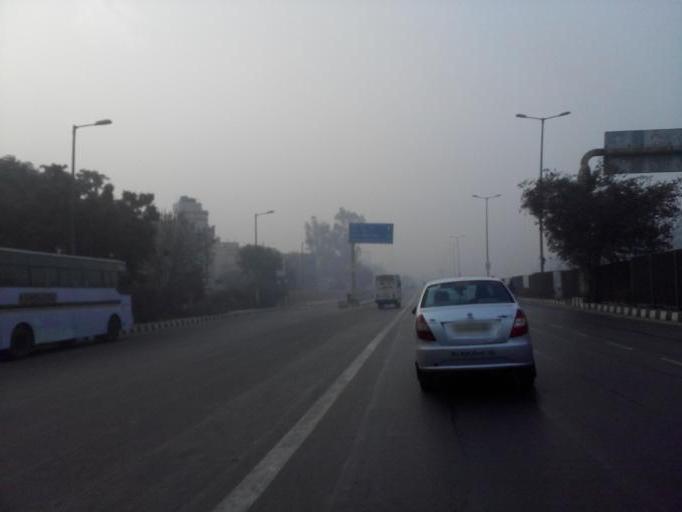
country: IN
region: Uttar Pradesh
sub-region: Gautam Buddha Nagar
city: Noida
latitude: 28.6588
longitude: 77.3200
